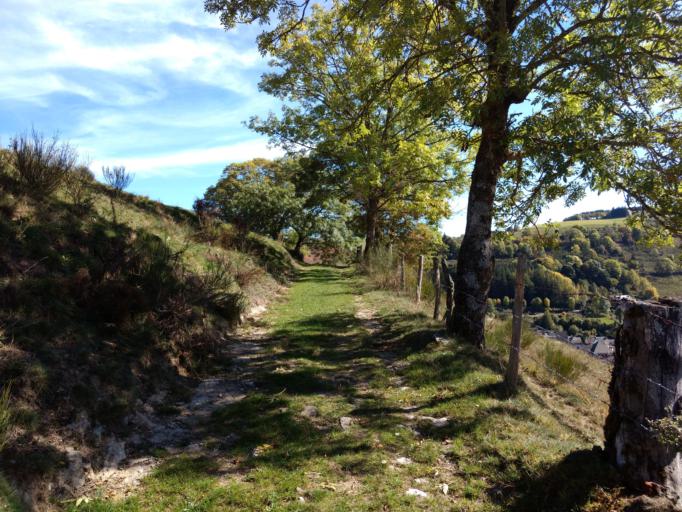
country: FR
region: Auvergne
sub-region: Departement du Cantal
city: Chaudes-Aigues
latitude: 44.8572
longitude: 3.0024
